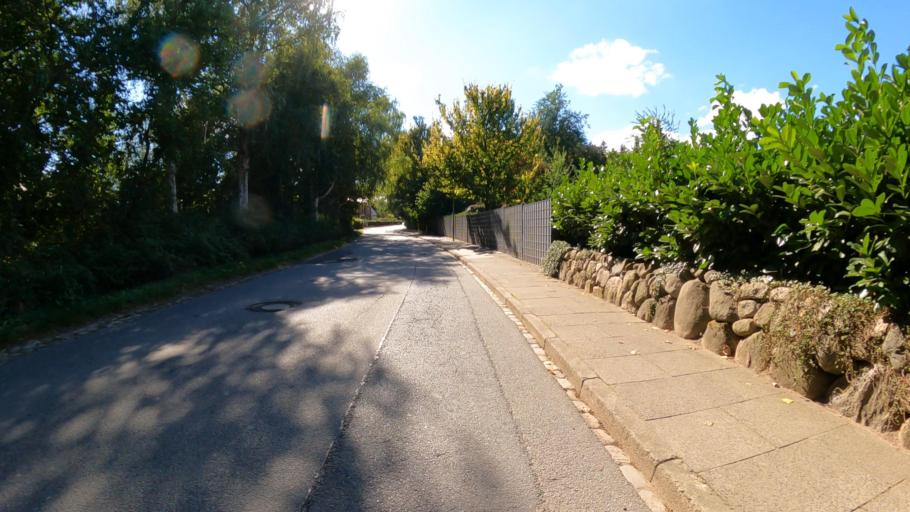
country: DE
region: Schleswig-Holstein
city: Stubben
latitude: 53.7322
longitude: 10.4287
